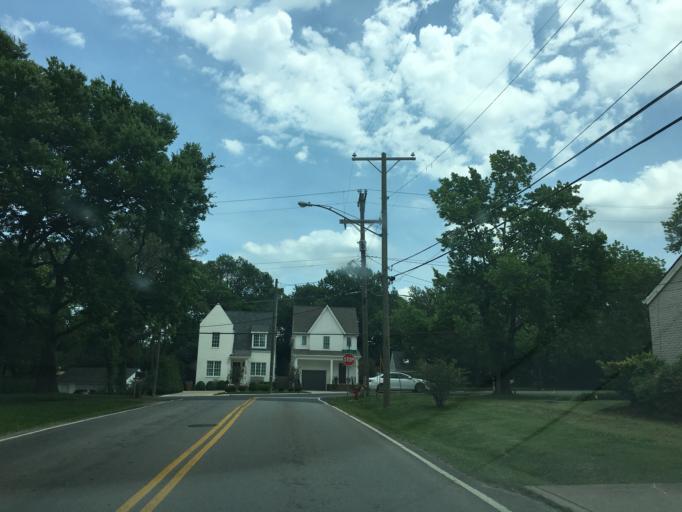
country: US
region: Tennessee
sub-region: Davidson County
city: Oak Hill
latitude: 36.1015
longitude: -86.8096
